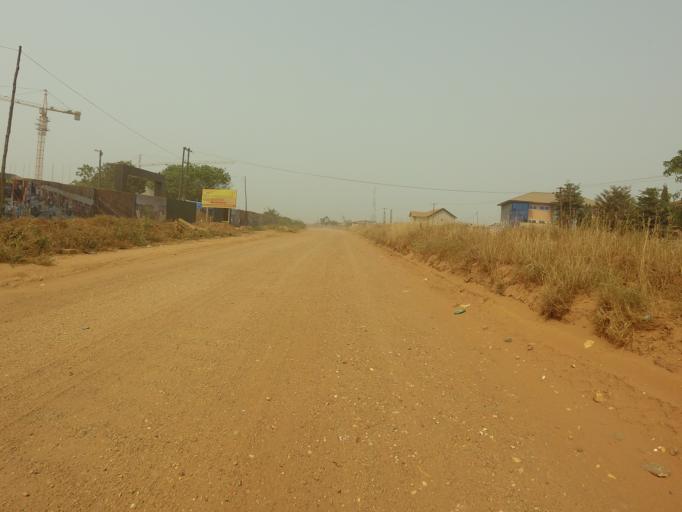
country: GH
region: Greater Accra
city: Medina Estates
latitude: 5.6334
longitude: -0.1248
